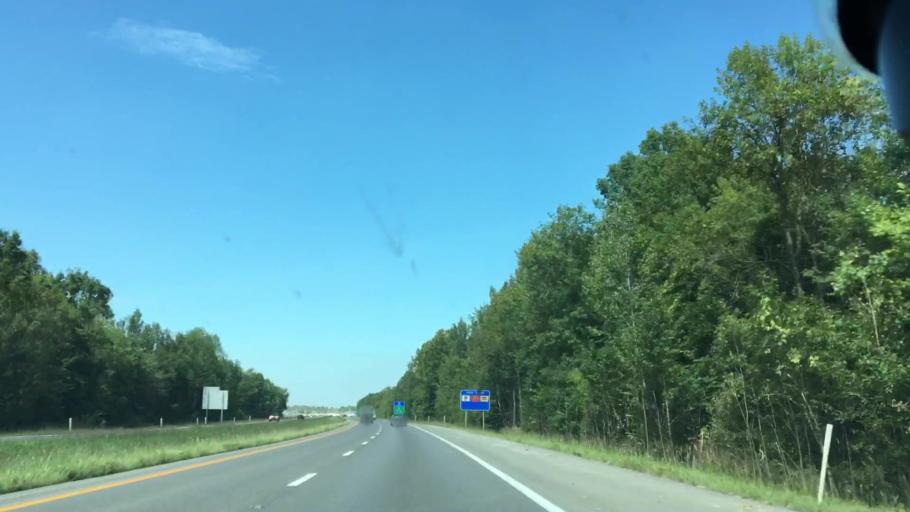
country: US
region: Kentucky
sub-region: Hopkins County
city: Madisonville
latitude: 37.3114
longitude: -87.4687
